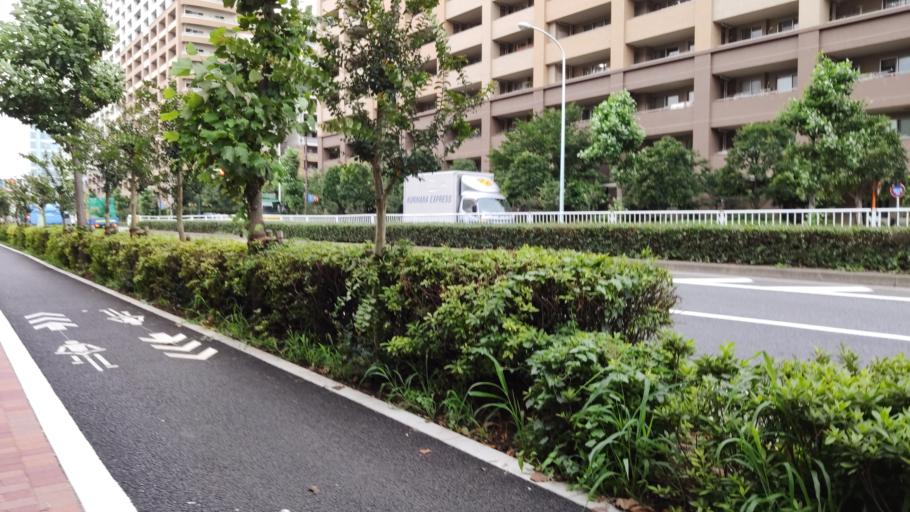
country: JP
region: Tokyo
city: Urayasu
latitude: 35.6660
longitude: 139.8354
